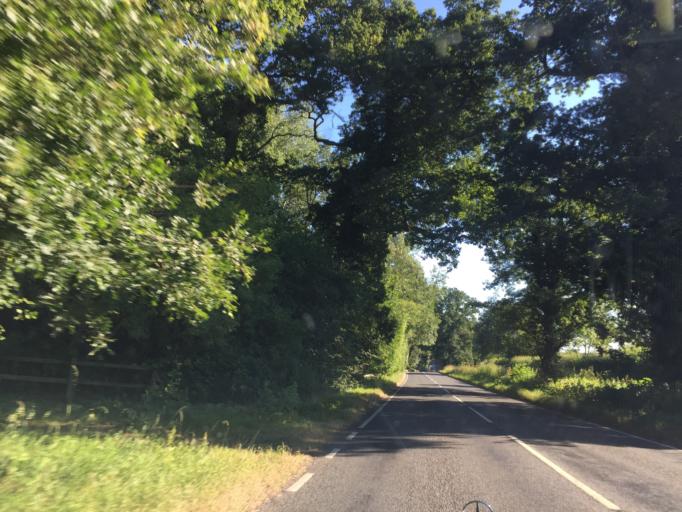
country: GB
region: England
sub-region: Warwickshire
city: Royal Leamington Spa
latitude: 52.3266
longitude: -1.5250
